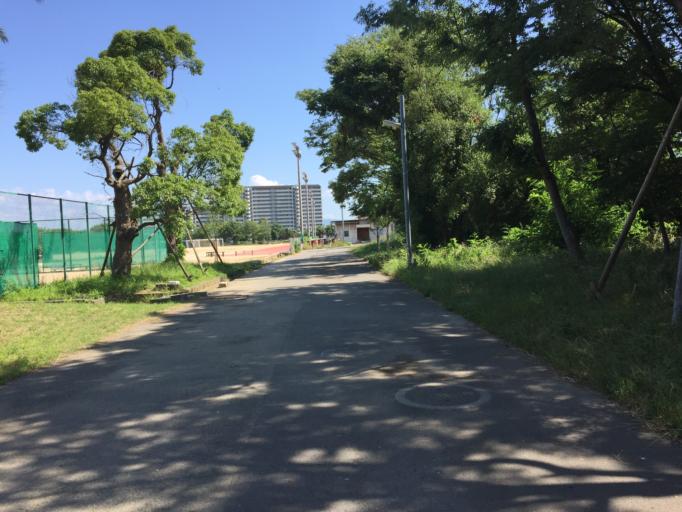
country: JP
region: Osaka
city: Sakai
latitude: 34.5896
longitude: 135.5031
